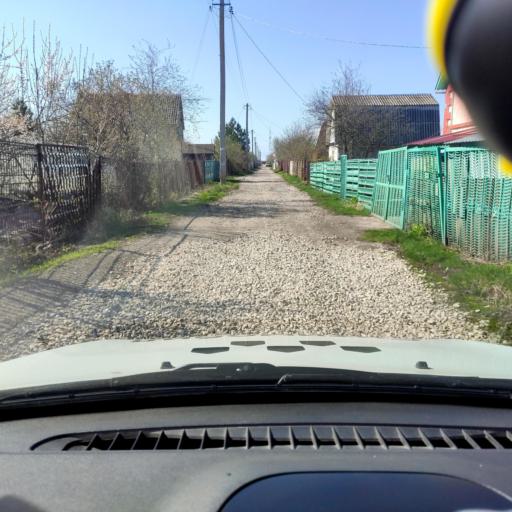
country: RU
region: Samara
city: Tol'yatti
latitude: 53.5955
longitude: 49.2941
